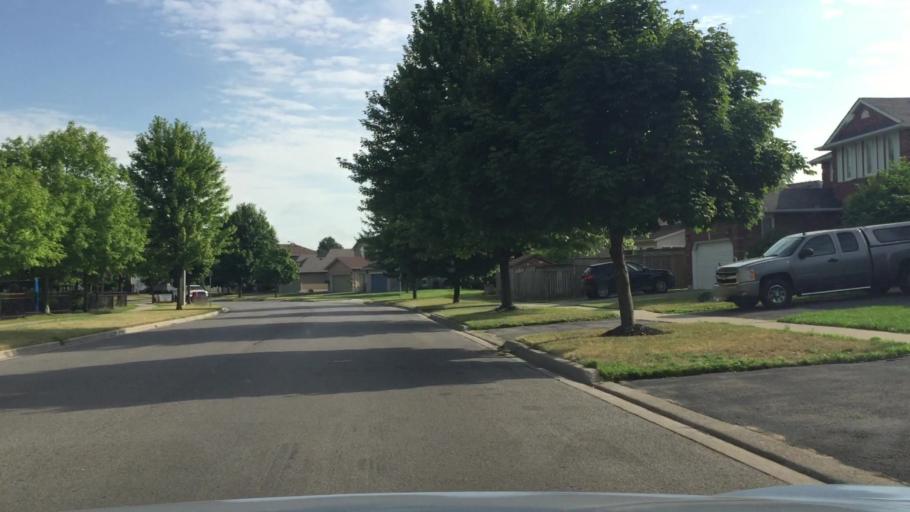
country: CA
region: Ontario
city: Oshawa
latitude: 43.9074
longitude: -78.7800
